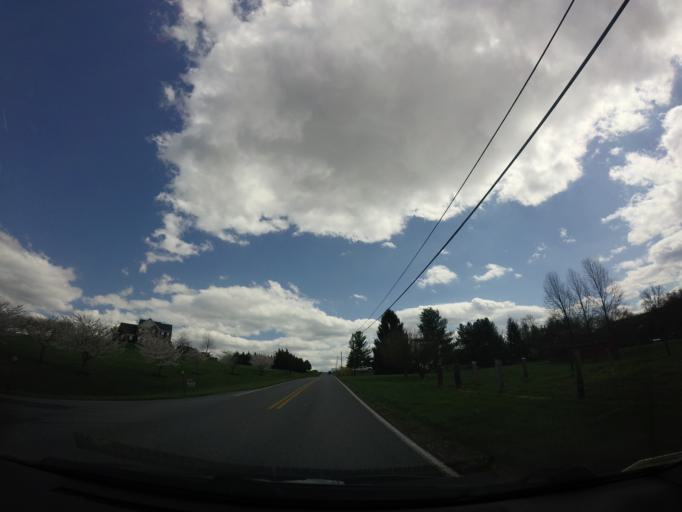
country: US
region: Maryland
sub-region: Washington County
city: Keedysville
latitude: 39.4294
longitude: -77.6760
